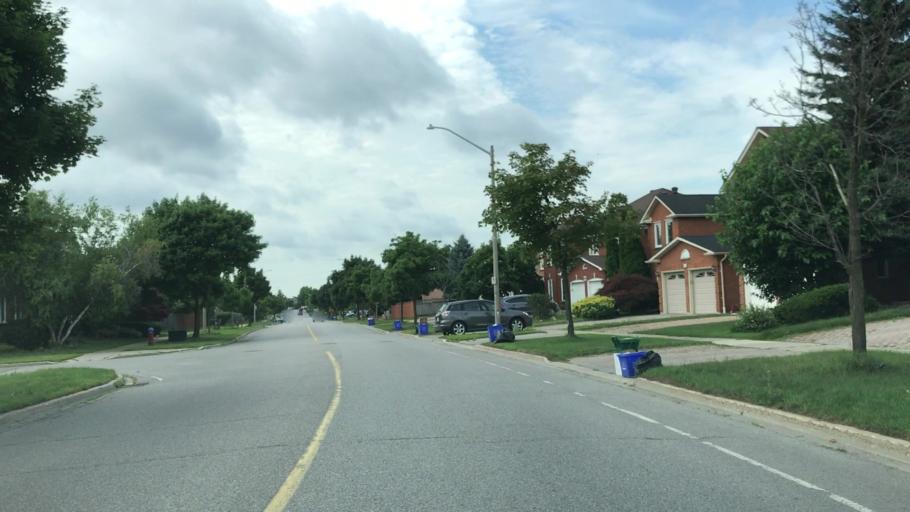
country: CA
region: Ontario
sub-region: York
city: Richmond Hill
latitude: 43.8561
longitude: -79.4014
